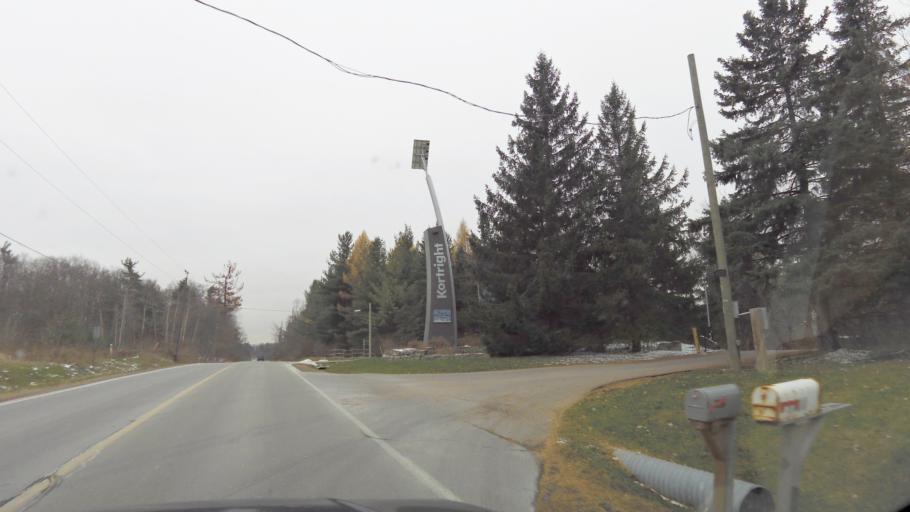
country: CA
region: Ontario
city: Vaughan
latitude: 43.8298
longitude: -79.5842
